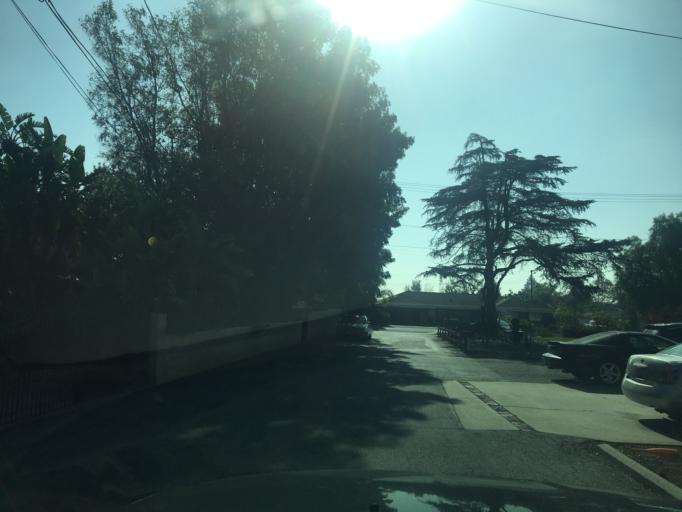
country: US
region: California
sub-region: Orange County
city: North Tustin
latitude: 33.7665
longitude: -117.8042
